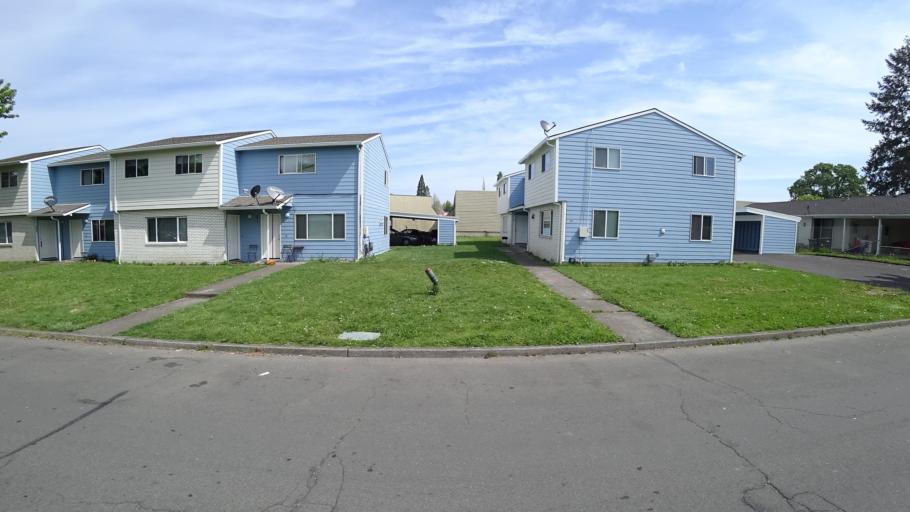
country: US
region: Oregon
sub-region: Washington County
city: Hillsboro
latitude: 45.5299
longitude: -122.9621
